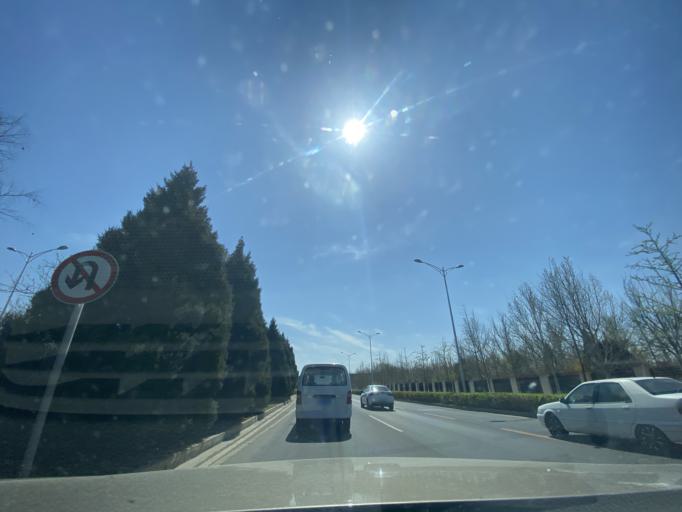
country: CN
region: Beijing
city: Sijiqing
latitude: 39.9374
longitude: 116.2409
